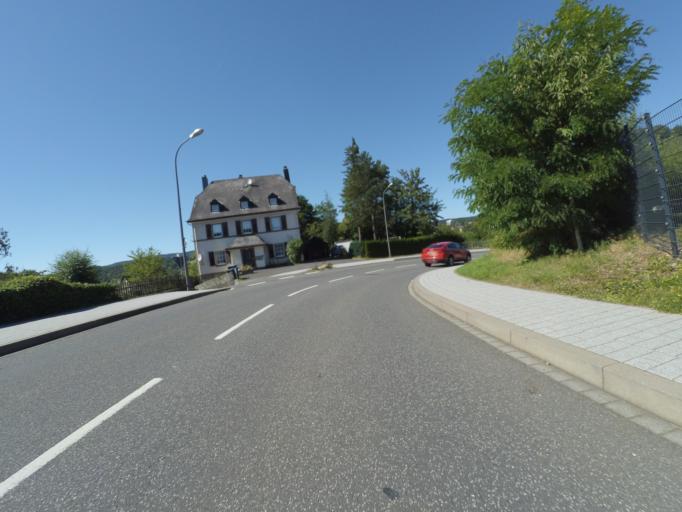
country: DE
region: Rheinland-Pfalz
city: Gerolstein
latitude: 50.2217
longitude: 6.6546
